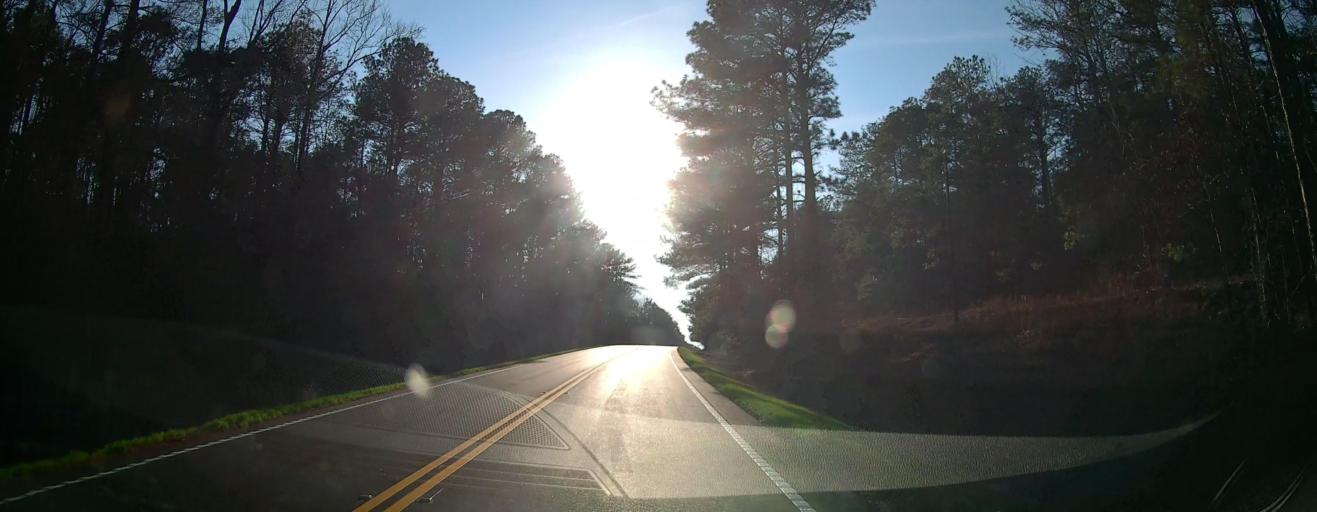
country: US
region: Georgia
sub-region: Harris County
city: Hamilton
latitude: 32.7420
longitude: -84.9507
